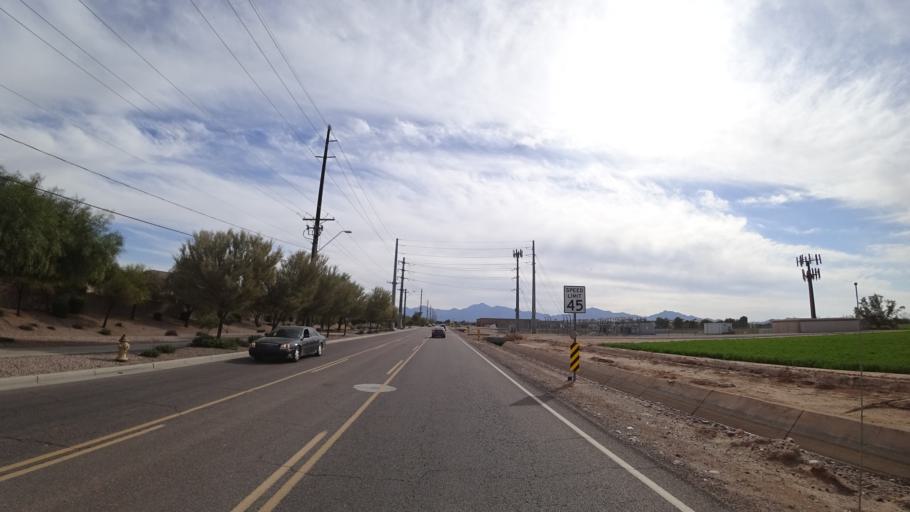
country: US
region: Arizona
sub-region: Maricopa County
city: Tolleson
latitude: 33.4271
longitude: -112.2554
